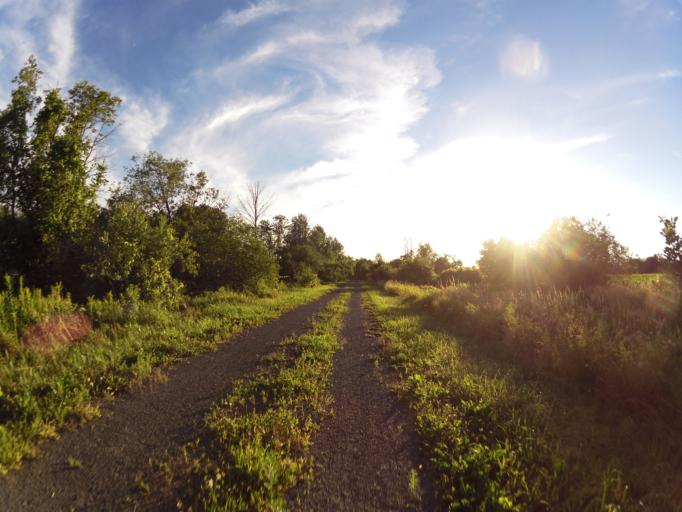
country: CA
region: Ontario
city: Ottawa
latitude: 45.4133
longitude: -75.5909
